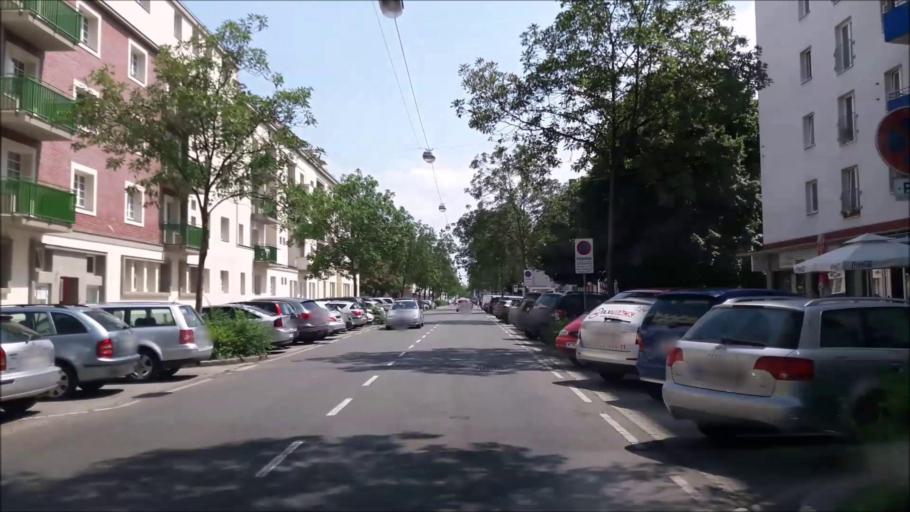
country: AT
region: Vienna
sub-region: Wien Stadt
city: Vienna
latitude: 48.2305
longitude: 16.4177
